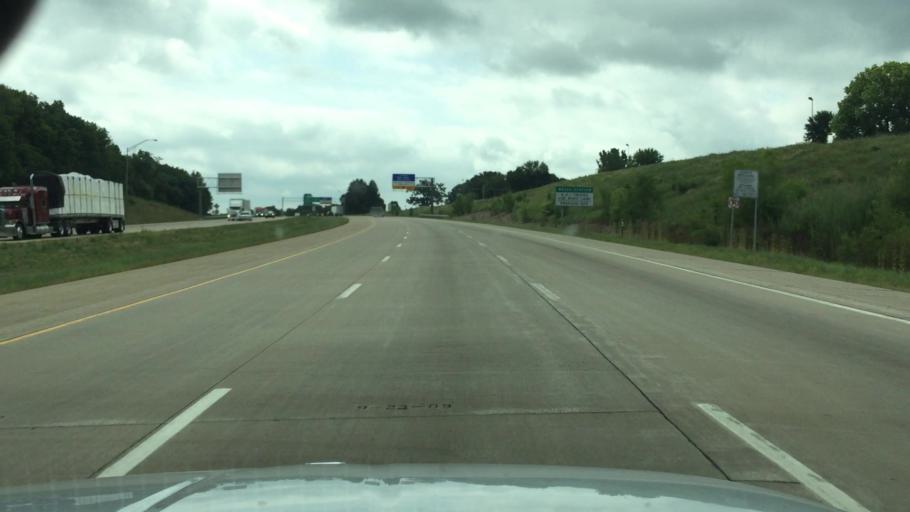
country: US
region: Iowa
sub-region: Scott County
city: Le Claire
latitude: 41.5709
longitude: -90.3592
